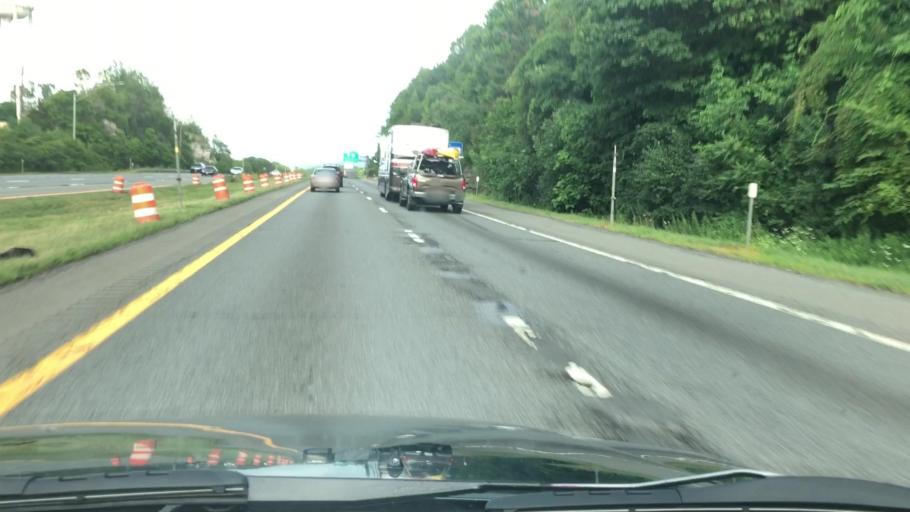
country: US
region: New York
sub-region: Orange County
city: Balmville
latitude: 41.5196
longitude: -74.0285
